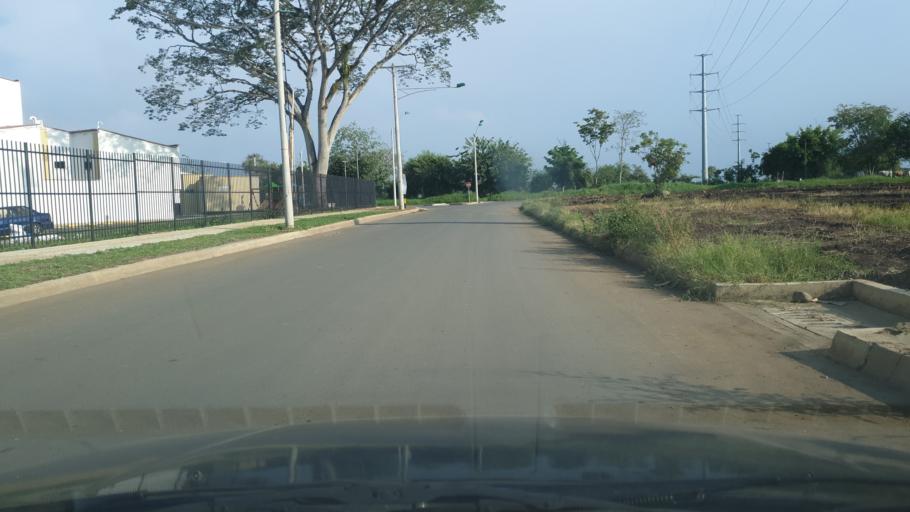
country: CO
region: Valle del Cauca
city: Jamundi
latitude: 3.3452
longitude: -76.5141
